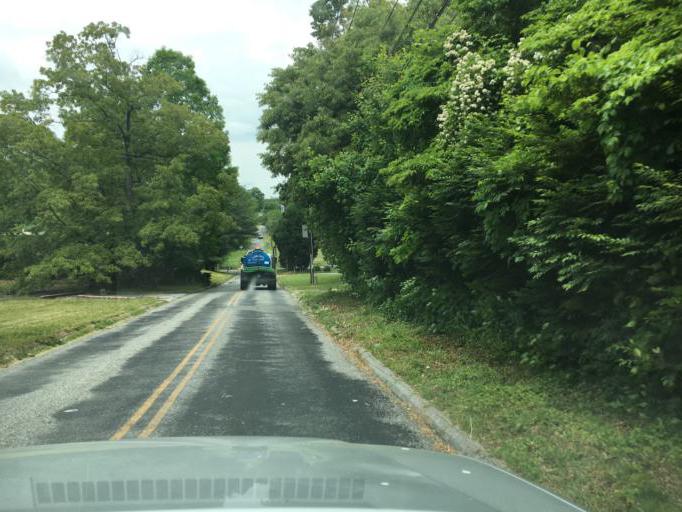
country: US
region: North Carolina
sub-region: Henderson County
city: Mountain Home
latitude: 35.3655
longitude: -82.4801
